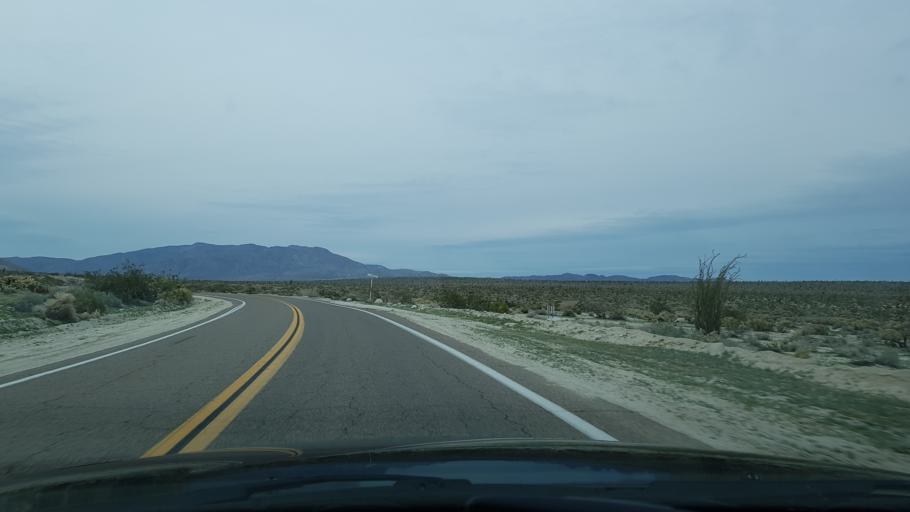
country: US
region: California
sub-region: San Diego County
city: Pine Valley
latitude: 32.8772
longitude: -116.2090
